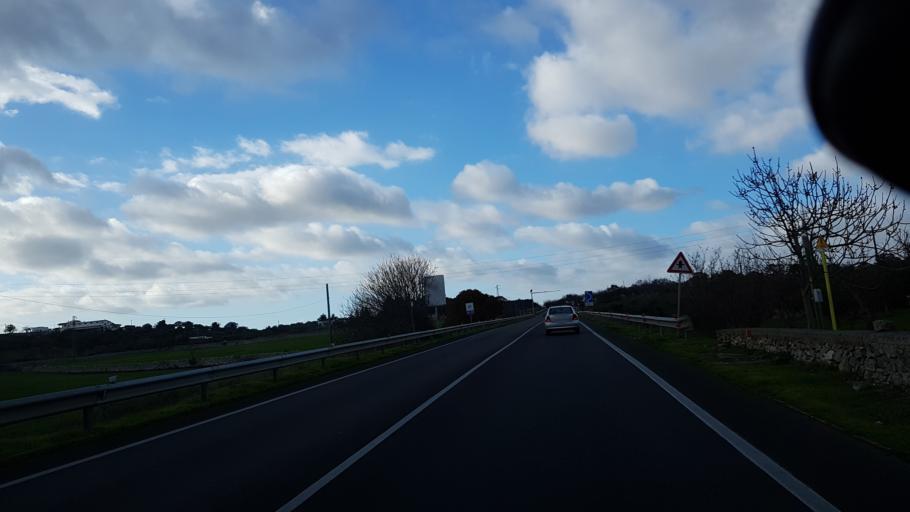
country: IT
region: Apulia
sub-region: Provincia di Bari
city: Castellana
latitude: 40.8269
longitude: 17.1837
